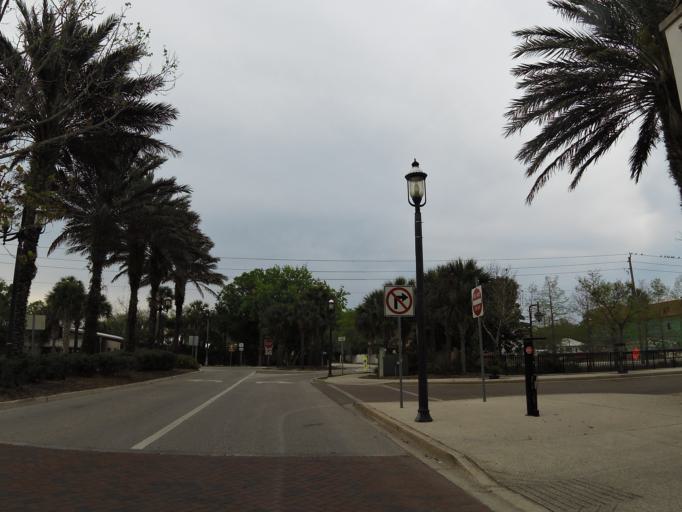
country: US
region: Florida
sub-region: Saint Johns County
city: Saint Augustine
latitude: 29.8988
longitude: -81.3166
